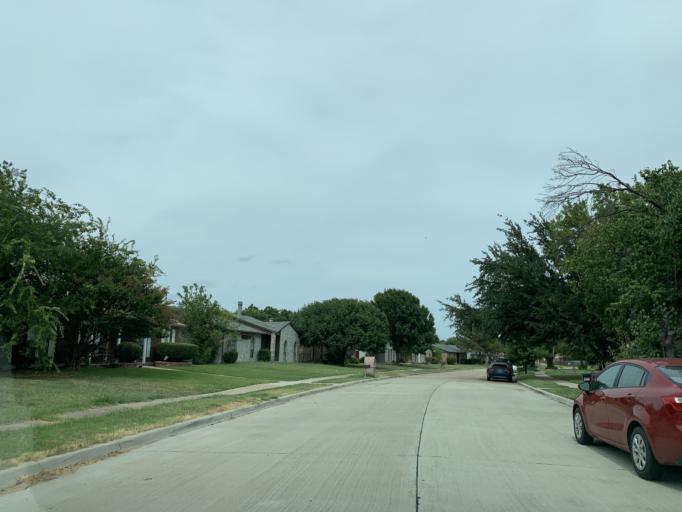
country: US
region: Texas
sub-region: Dallas County
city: Cedar Hill
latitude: 32.6530
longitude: -97.0304
